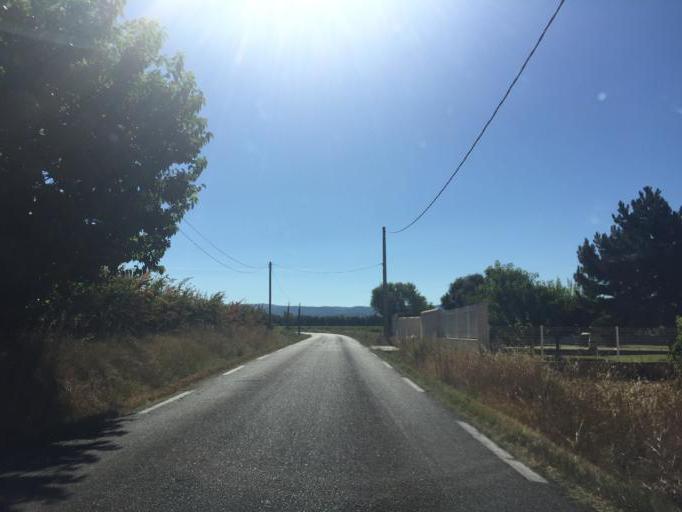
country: FR
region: Provence-Alpes-Cote d'Azur
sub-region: Departement du Vaucluse
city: Saint-Didier
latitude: 44.0267
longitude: 5.0964
